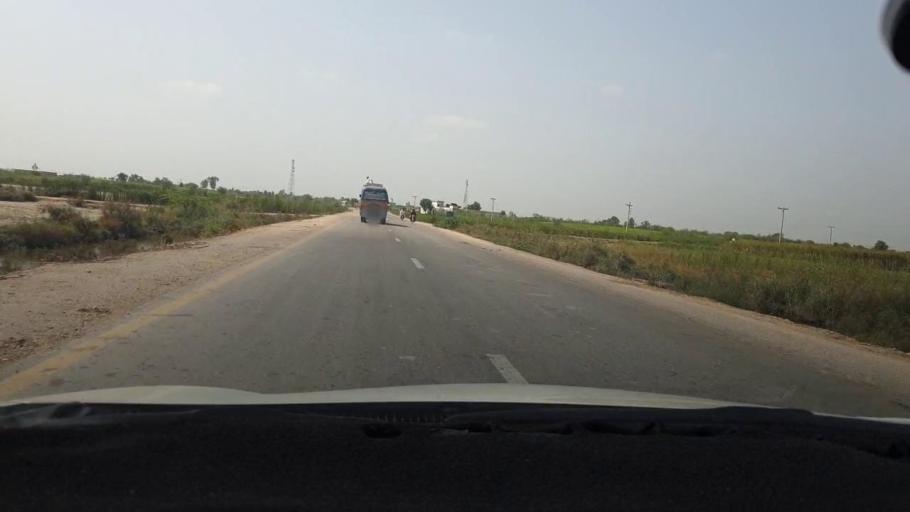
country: PK
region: Sindh
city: Mirpur Khas
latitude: 25.5779
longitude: 69.0708
